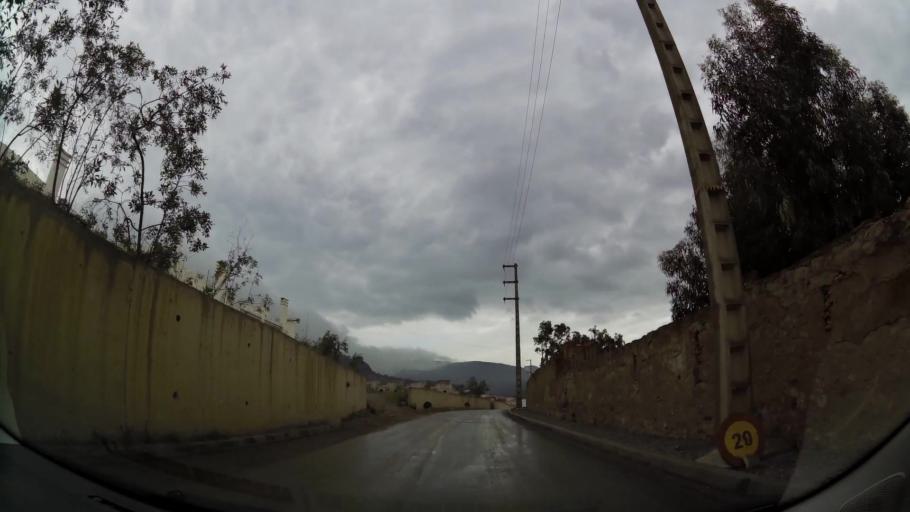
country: MA
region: Oriental
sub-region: Nador
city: Nador
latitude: 35.1494
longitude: -3.0080
